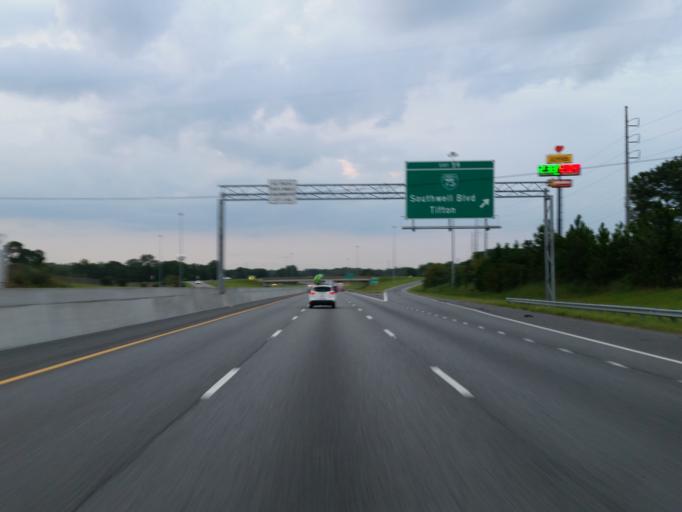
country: US
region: Georgia
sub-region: Tift County
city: Unionville
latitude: 31.4122
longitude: -83.5039
